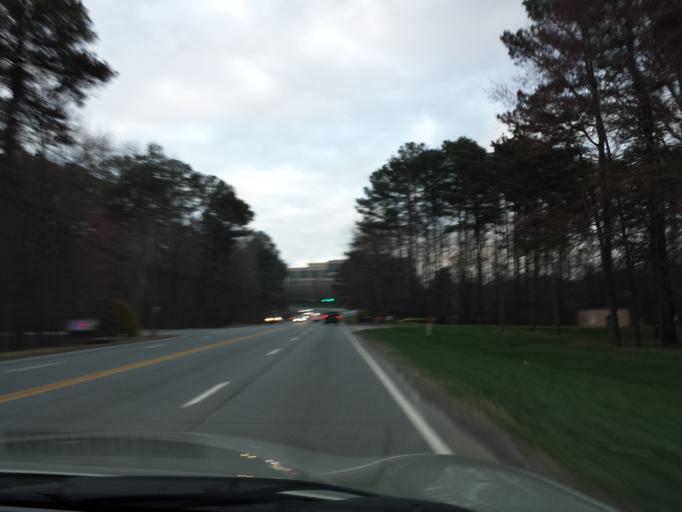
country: US
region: Georgia
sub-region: Fulton County
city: Alpharetta
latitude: 34.0591
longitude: -84.2951
